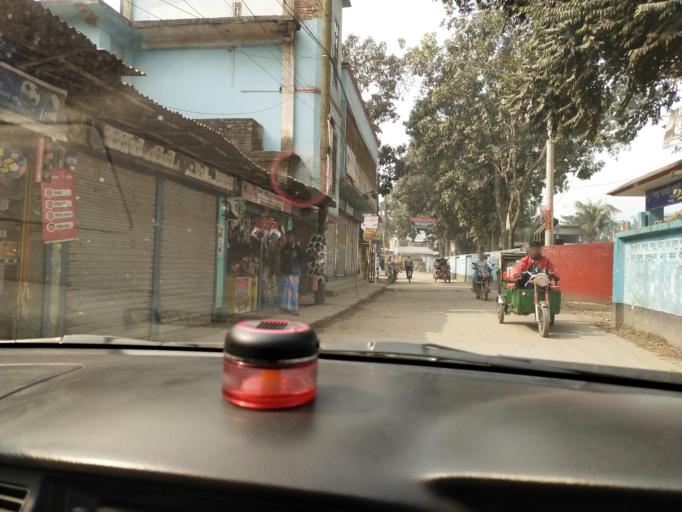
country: BD
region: Dhaka
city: Narsingdi
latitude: 24.0388
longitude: 90.7364
